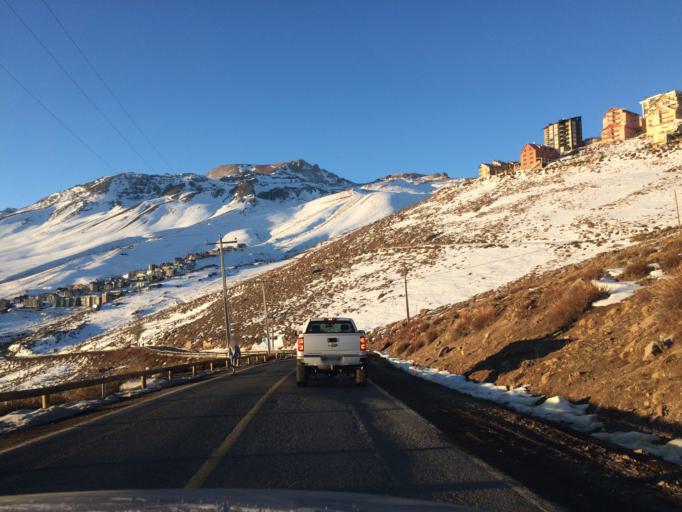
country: CL
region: Santiago Metropolitan
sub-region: Provincia de Santiago
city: Villa Presidente Frei, Nunoa, Santiago, Chile
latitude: -33.3476
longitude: -70.2956
